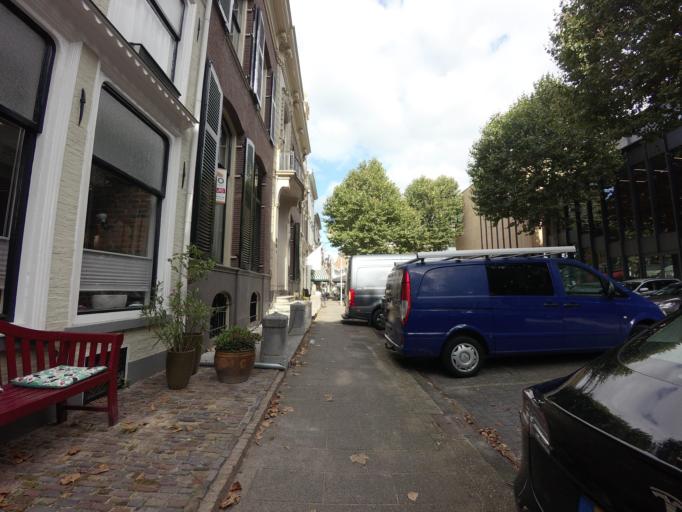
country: NL
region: Overijssel
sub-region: Gemeente Deventer
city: Deventer
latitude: 52.2531
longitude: 6.1550
